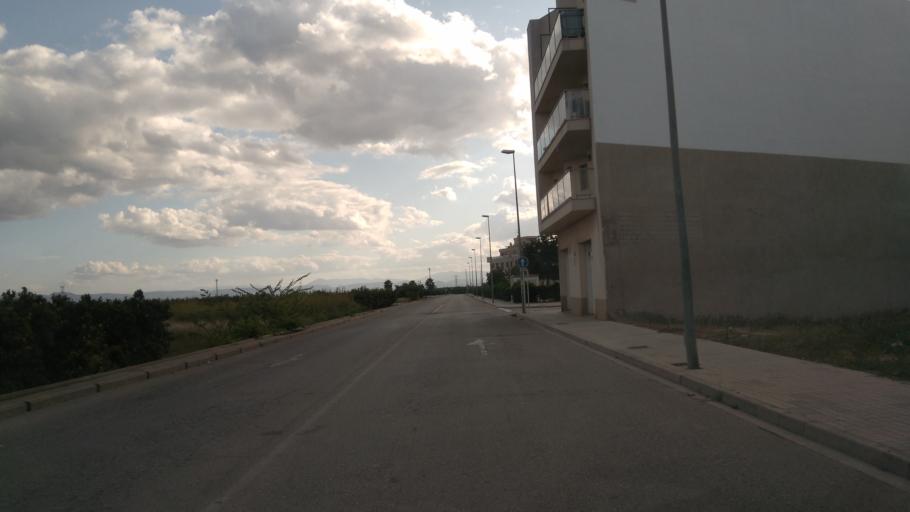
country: ES
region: Valencia
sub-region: Provincia de Valencia
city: L'Alcudia
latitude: 39.1941
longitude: -0.4991
